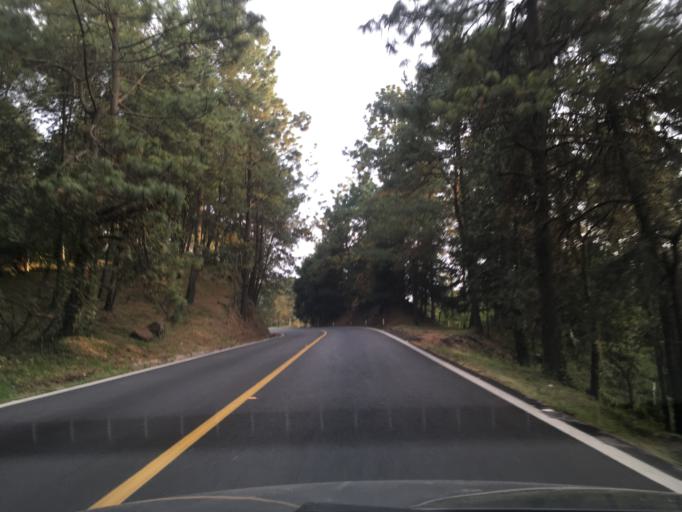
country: MX
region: Michoacan
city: Tingambato
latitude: 19.4979
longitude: -101.8271
